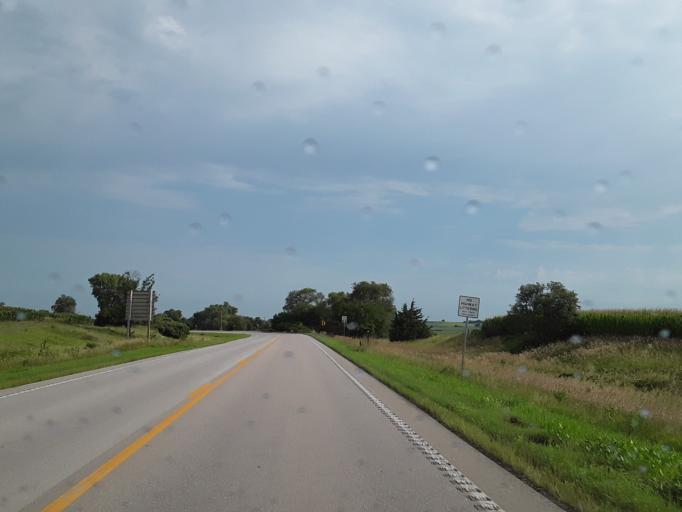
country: US
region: Nebraska
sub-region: Saunders County
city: Ashland
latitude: 41.0938
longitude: -96.4259
